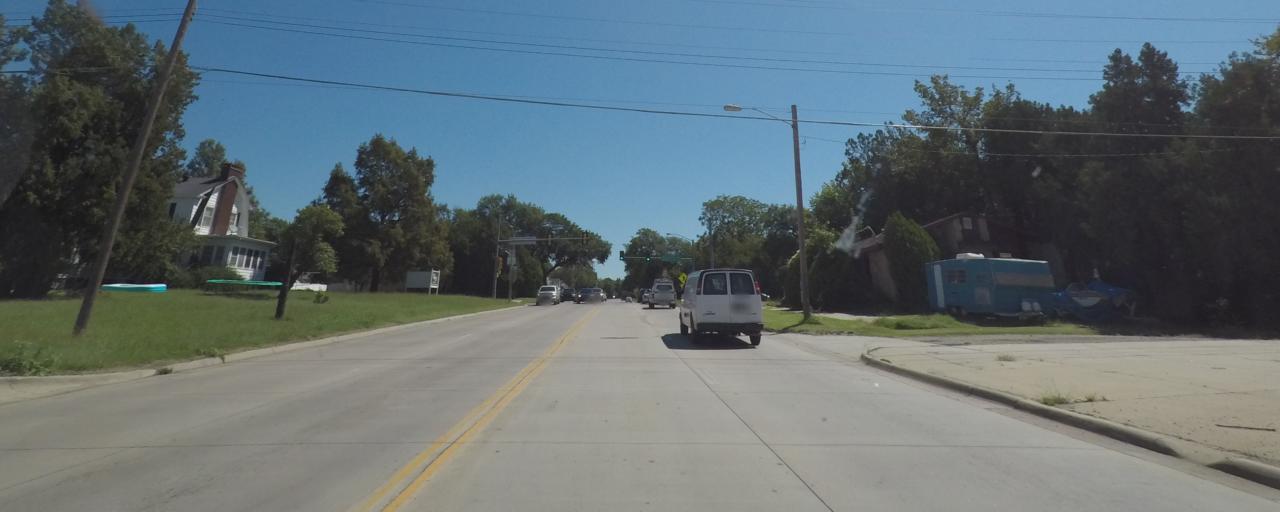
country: US
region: Kansas
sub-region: Sumner County
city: Wellington
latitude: 37.2745
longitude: -97.3993
